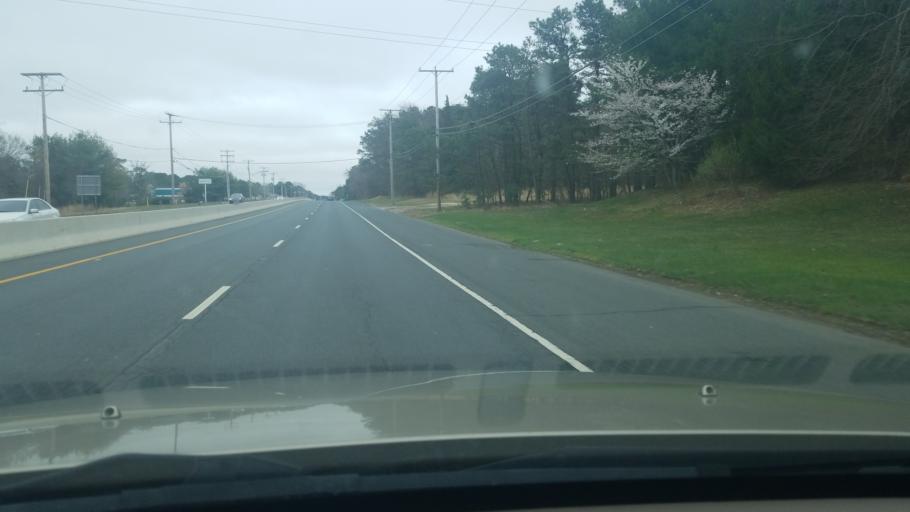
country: US
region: New Jersey
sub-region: Ocean County
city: Leisure Knoll
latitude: 39.9999
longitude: -74.2869
